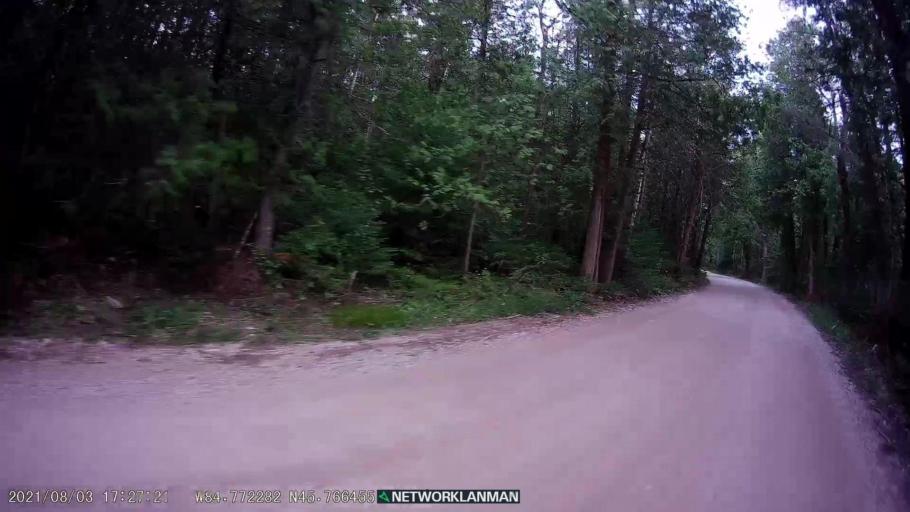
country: US
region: Michigan
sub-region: Mackinac County
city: Saint Ignace
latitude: 45.7664
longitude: -84.7722
